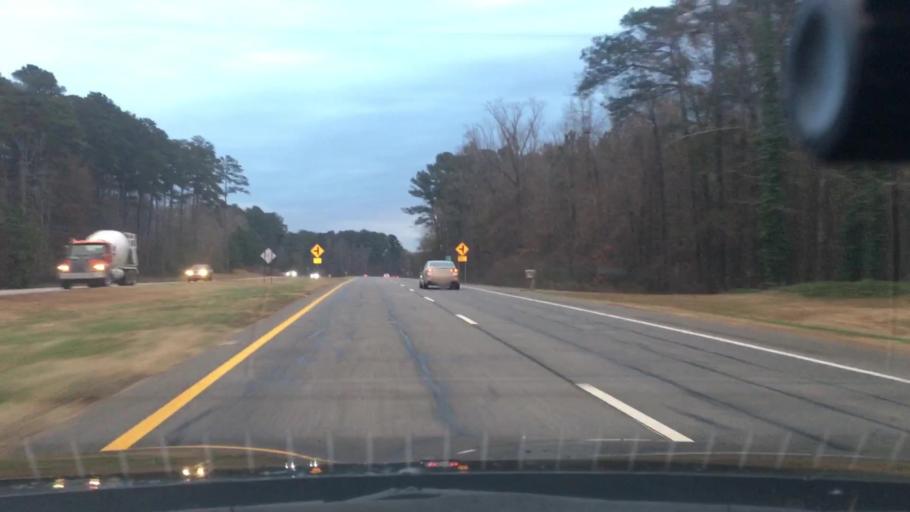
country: US
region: Georgia
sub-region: Fayette County
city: Peachtree City
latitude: 33.4017
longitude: -84.6373
